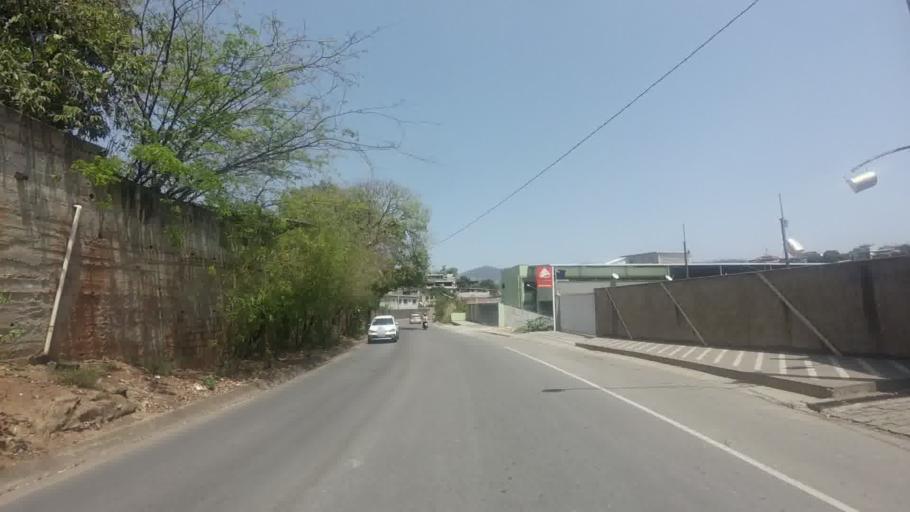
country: BR
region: Espirito Santo
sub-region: Cachoeiro De Itapemirim
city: Cachoeiro de Itapemirim
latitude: -20.8486
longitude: -41.1472
